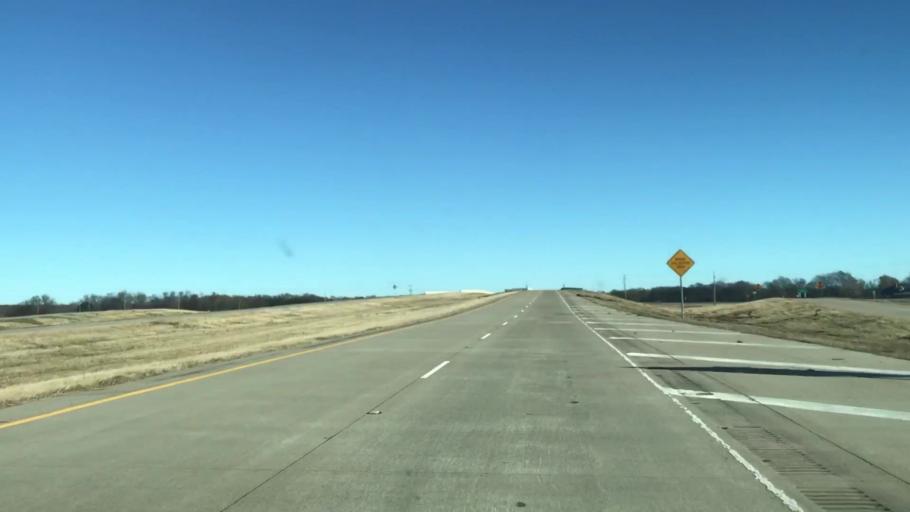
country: US
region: Louisiana
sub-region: Caddo Parish
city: Vivian
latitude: 32.8481
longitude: -93.8662
